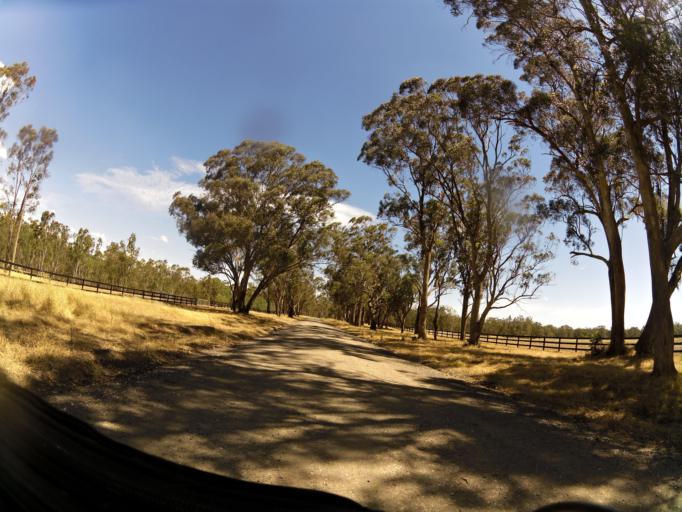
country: AU
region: Victoria
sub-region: Campaspe
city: Kyabram
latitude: -36.8266
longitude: 145.0782
